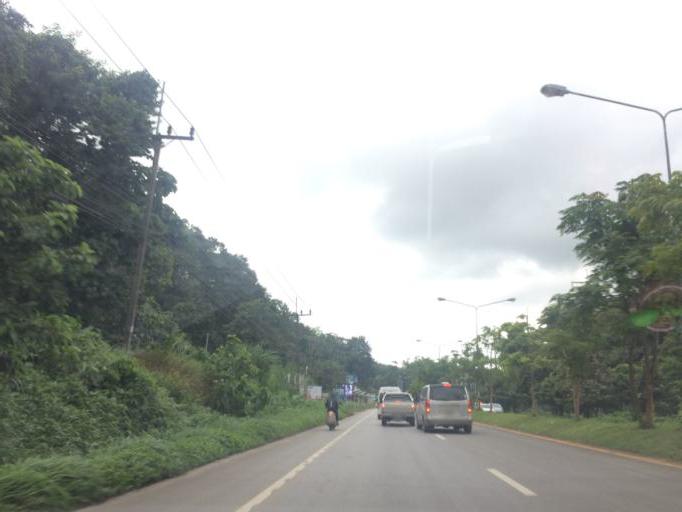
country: TH
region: Chiang Rai
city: Mae Chan
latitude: 20.1168
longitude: 99.8717
